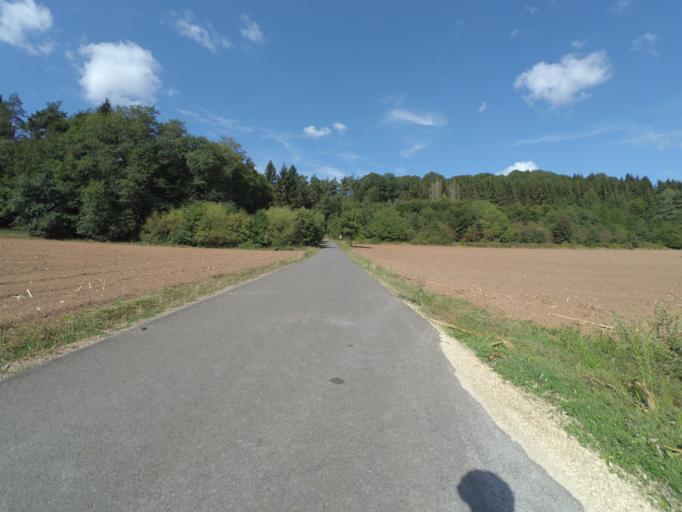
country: DE
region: Rheinland-Pfalz
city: Trassem
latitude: 49.5805
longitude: 6.5186
